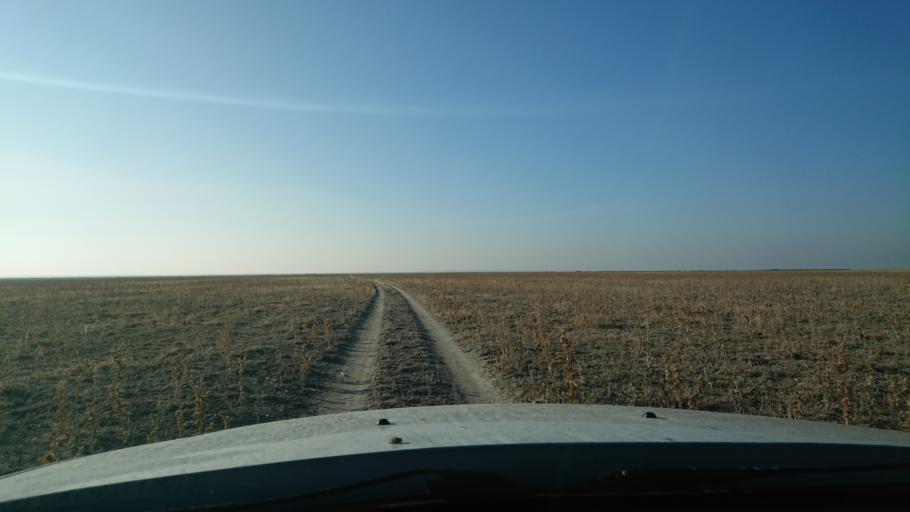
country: TR
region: Aksaray
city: Sultanhani
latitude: 38.3720
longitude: 33.5414
